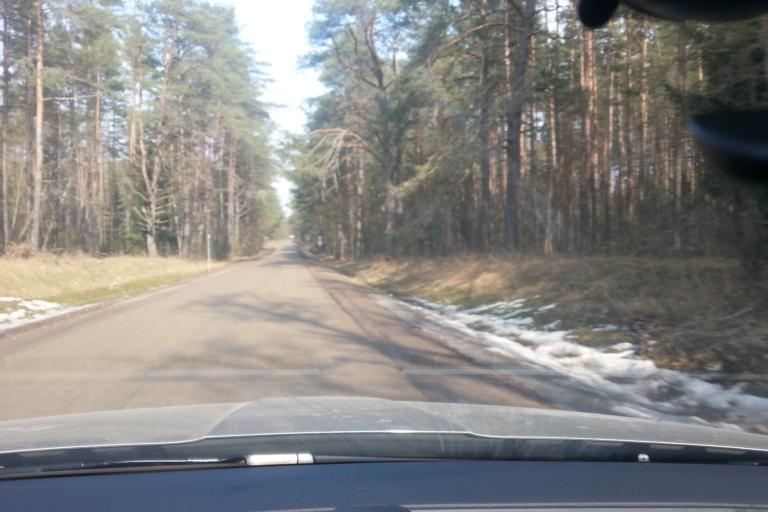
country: LT
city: Trakai
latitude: 54.5085
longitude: 24.9844
